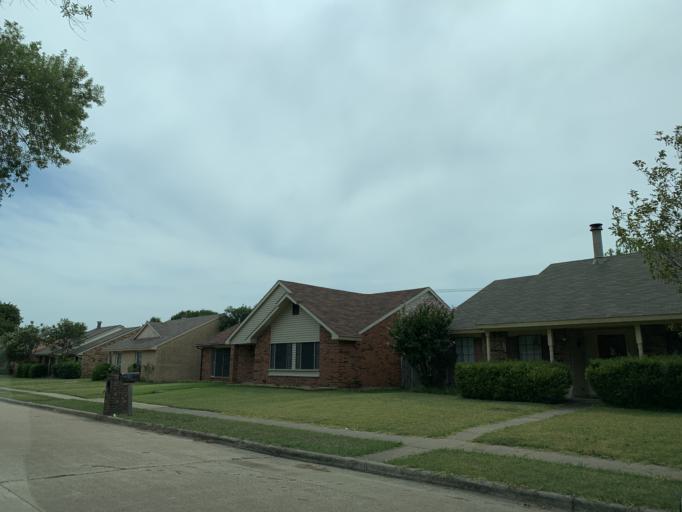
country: US
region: Texas
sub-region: Dallas County
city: Grand Prairie
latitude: 32.6525
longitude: -97.0345
